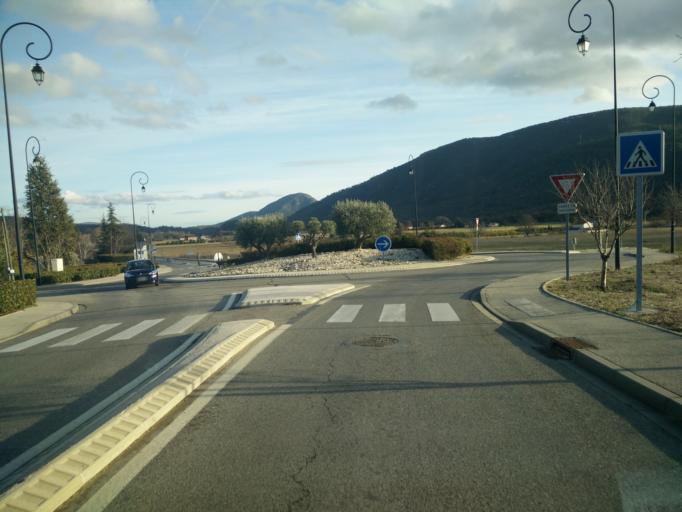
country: FR
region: Provence-Alpes-Cote d'Azur
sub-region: Departement du Var
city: Signes
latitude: 43.2897
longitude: 5.8708
